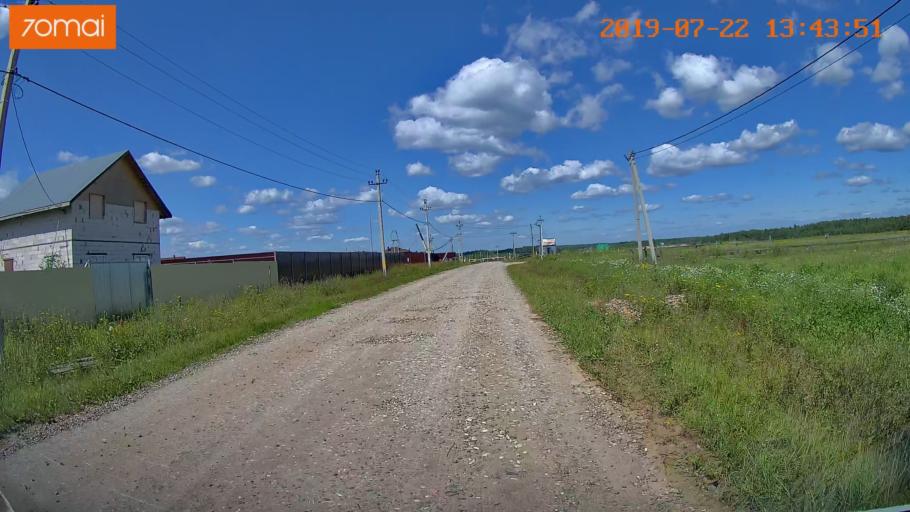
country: RU
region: Ivanovo
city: Novo-Talitsy
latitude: 57.0843
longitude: 40.8740
